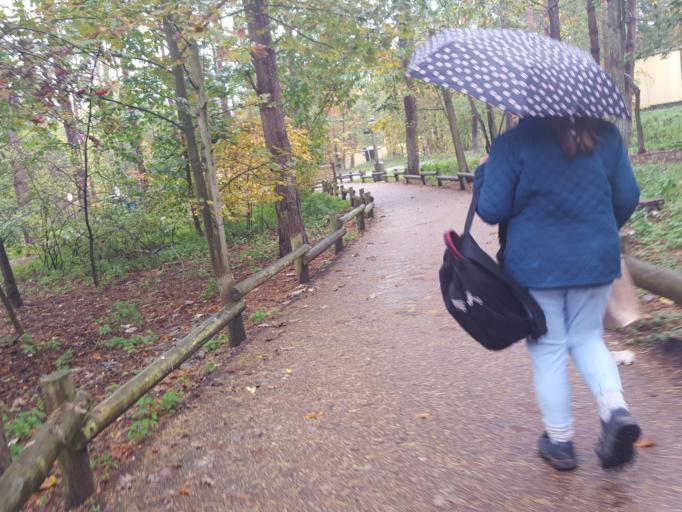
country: GB
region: England
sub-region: Norfolk
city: Weeting
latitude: 52.3924
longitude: 0.6370
